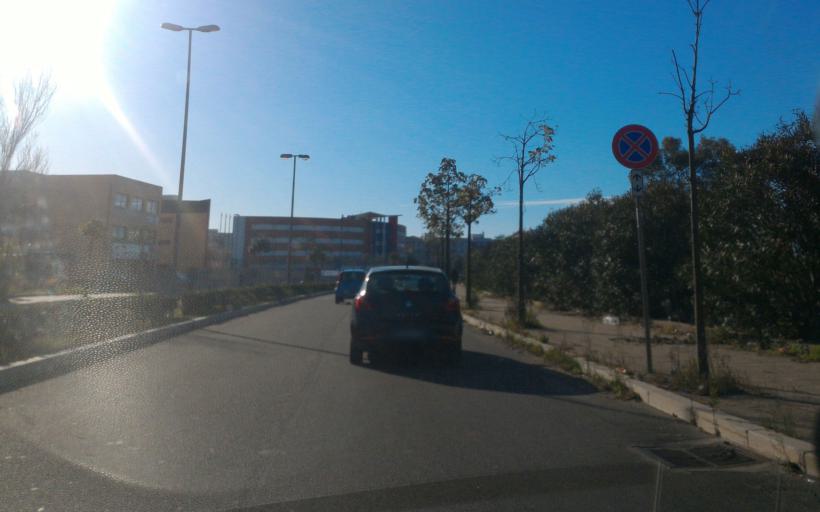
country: IT
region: Calabria
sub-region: Provincia di Crotone
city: Crotone
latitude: 39.0697
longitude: 17.1137
